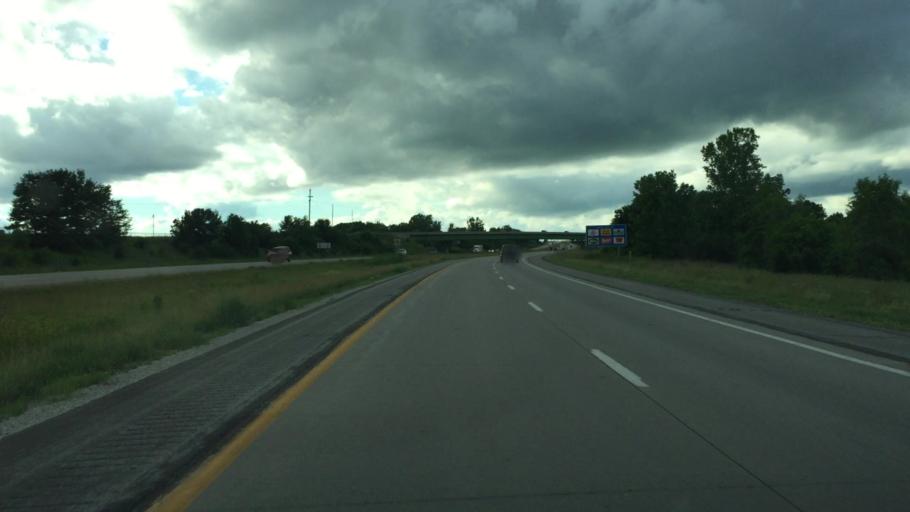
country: US
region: Iowa
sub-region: Polk County
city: Altoona
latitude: 41.6297
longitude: -93.5007
